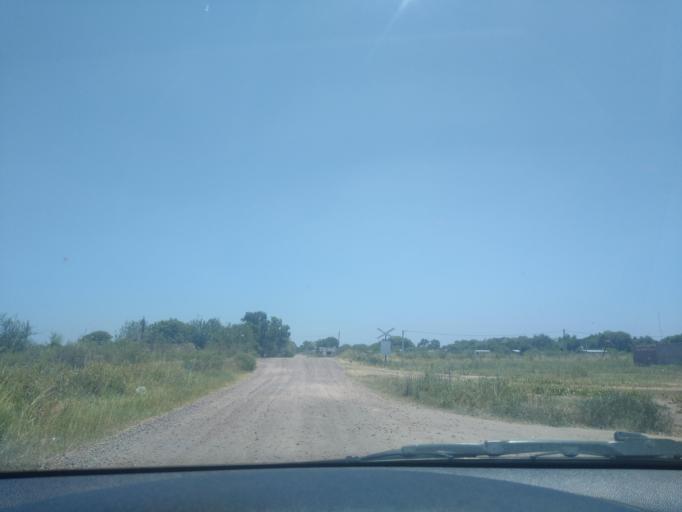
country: AR
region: Chaco
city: Puerto Tirol
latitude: -27.3807
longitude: -59.0940
